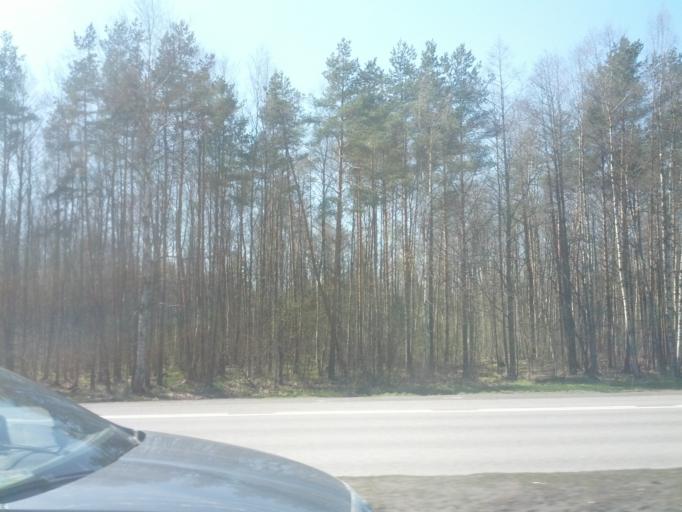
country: RU
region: St.-Petersburg
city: Razliv
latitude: 60.0752
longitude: 29.9651
